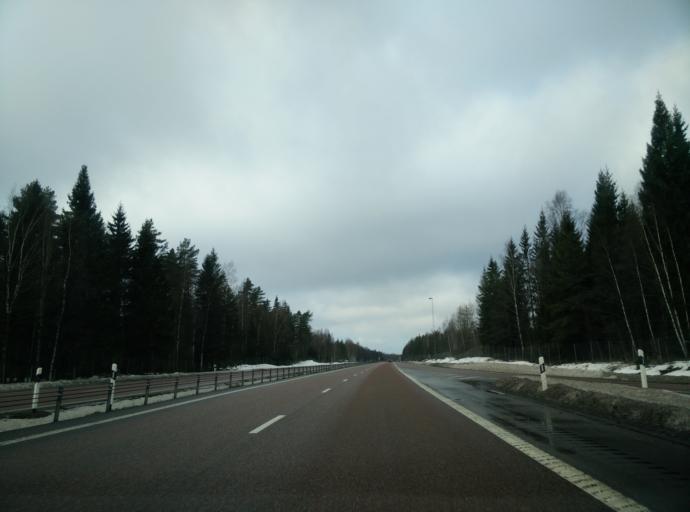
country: SE
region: Gaevleborg
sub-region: Sandvikens Kommun
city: Sandviken
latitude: 60.6250
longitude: 16.8881
